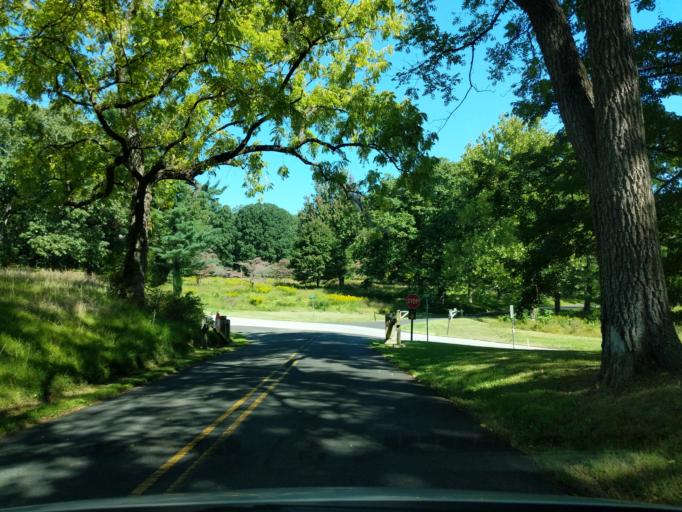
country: US
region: Pennsylvania
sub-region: Chester County
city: Chesterbrook
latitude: 40.0973
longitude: -75.4524
